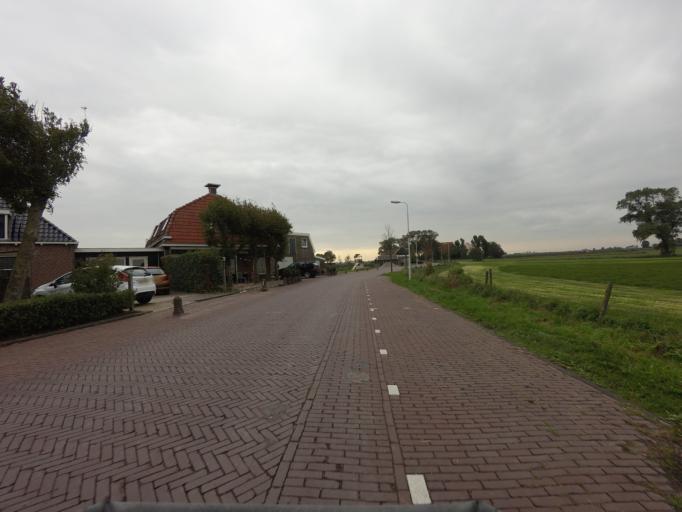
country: NL
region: Friesland
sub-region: Sudwest Fryslan
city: Bolsward
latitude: 53.0163
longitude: 5.5492
